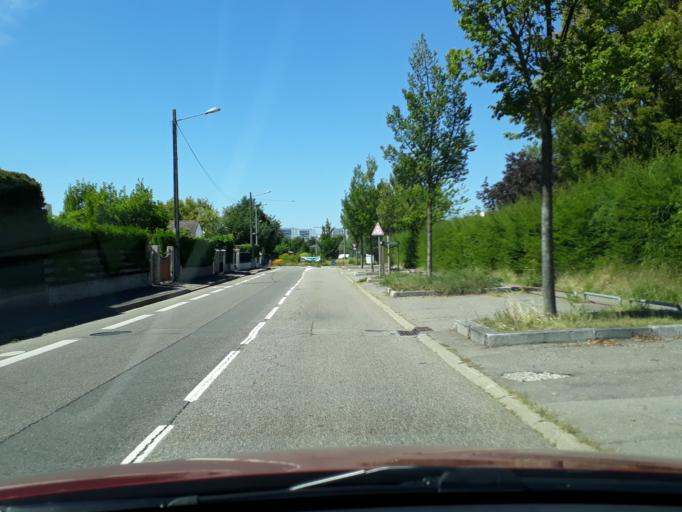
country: FR
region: Rhone-Alpes
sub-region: Departement du Rhone
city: Saint-Priest
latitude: 45.6925
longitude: 4.9590
